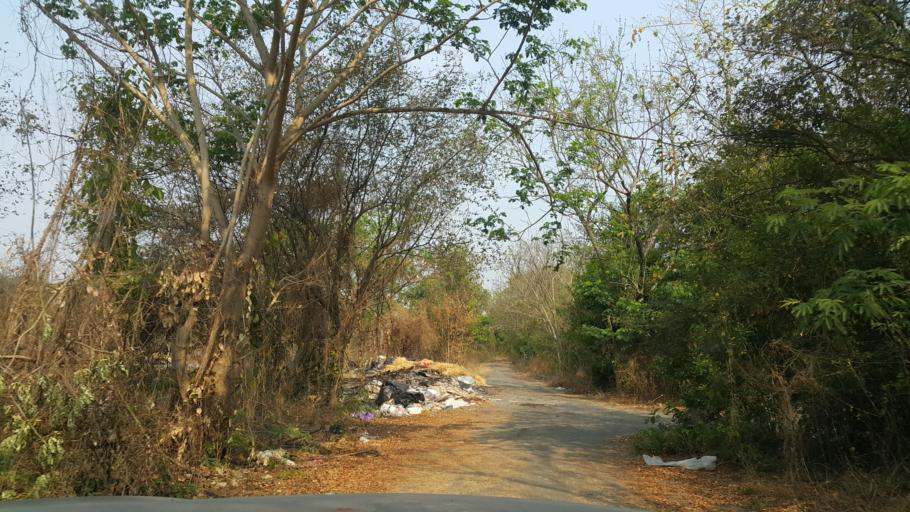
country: TH
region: Chiang Mai
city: San Kamphaeng
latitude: 18.7628
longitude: 99.1108
